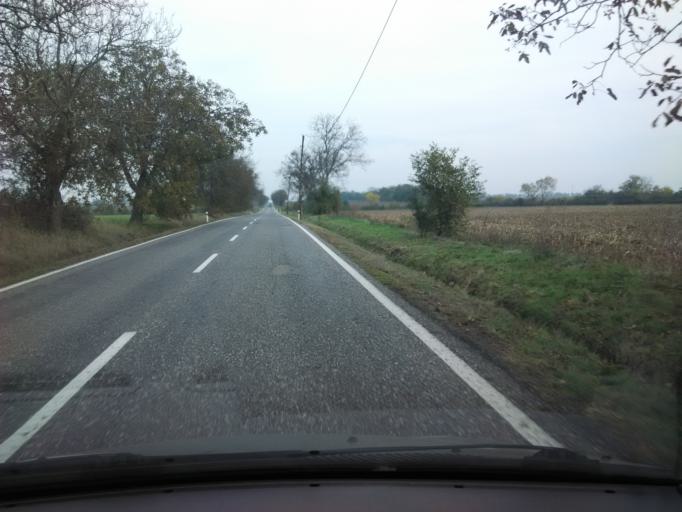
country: SK
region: Nitriansky
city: Zeliezovce
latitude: 48.0644
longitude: 18.5147
